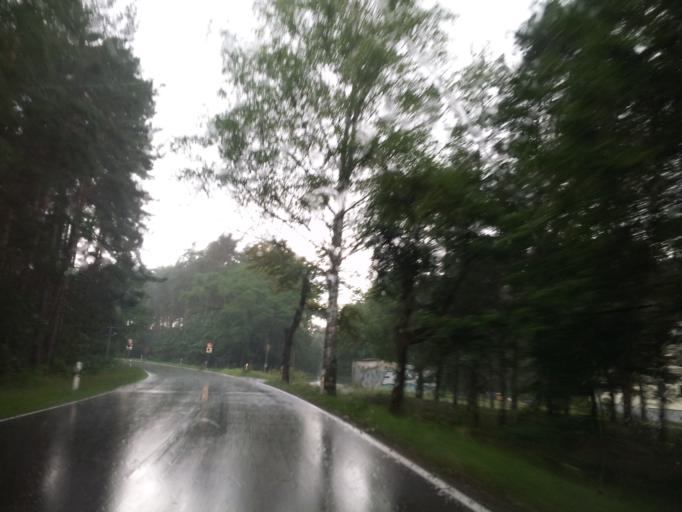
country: DE
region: Brandenburg
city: Wollin
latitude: 52.2765
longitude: 12.4606
